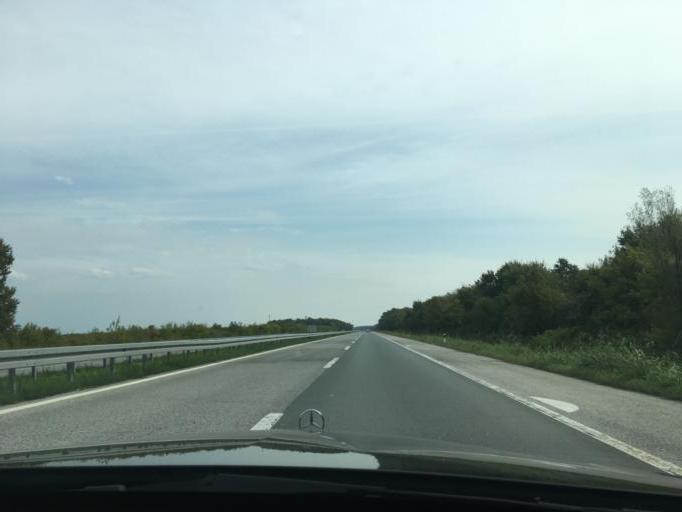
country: RS
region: Autonomna Pokrajina Vojvodina
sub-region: Sremski Okrug
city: Sid
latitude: 45.0443
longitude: 19.2444
